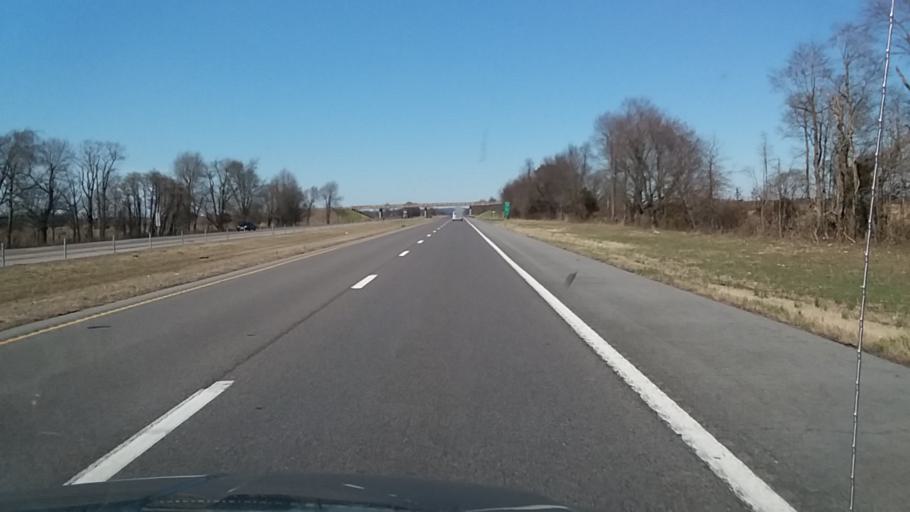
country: US
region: Missouri
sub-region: Scott County
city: Benton
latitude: 37.0362
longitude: -89.5352
